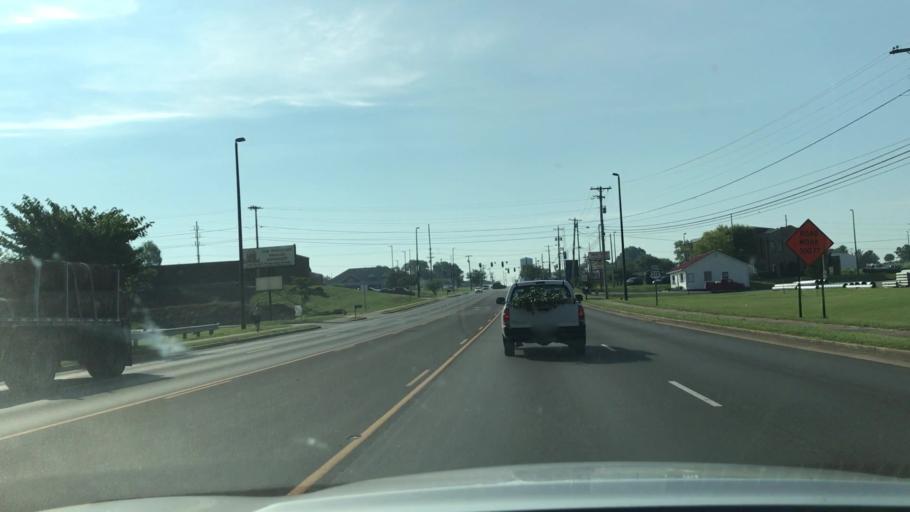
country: US
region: Kentucky
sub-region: Barren County
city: Glasgow
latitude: 37.0035
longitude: -85.9289
